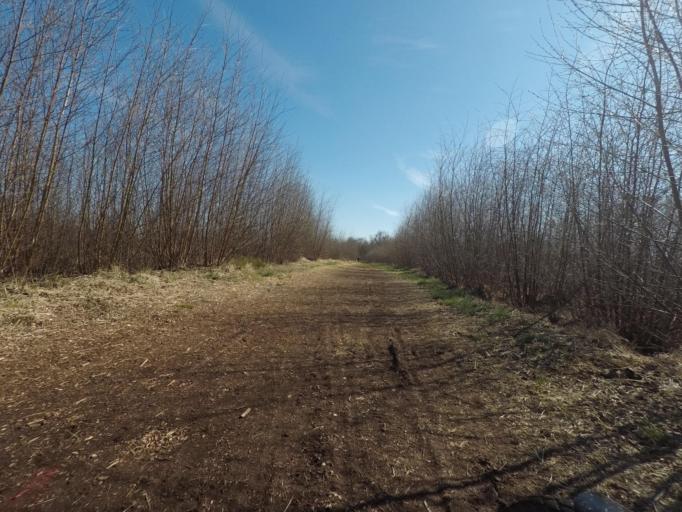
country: DE
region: Hamburg
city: Langenhorn
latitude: 53.6537
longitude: 9.9726
